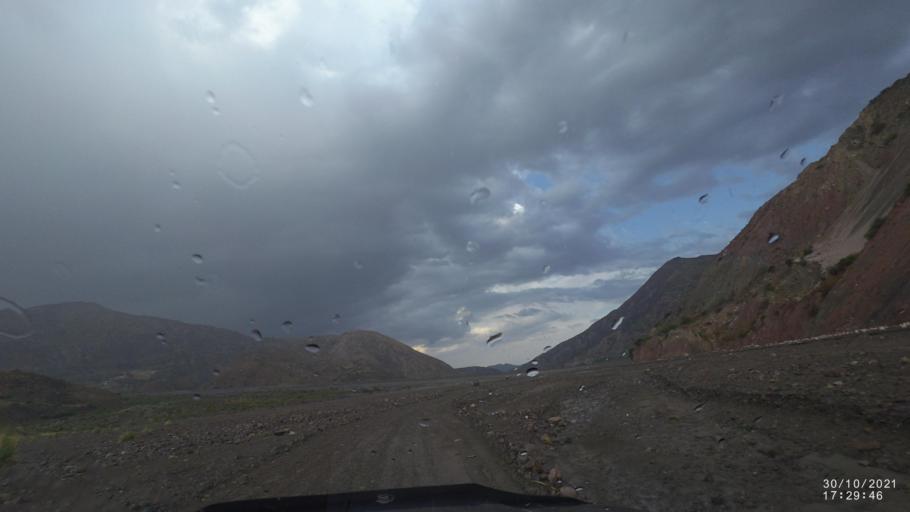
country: BO
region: Cochabamba
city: Sipe Sipe
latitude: -17.5234
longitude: -66.6011
